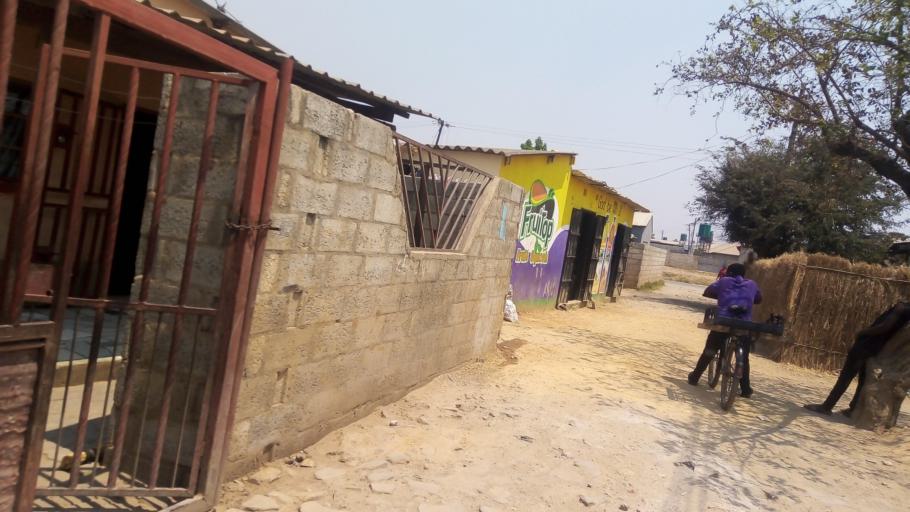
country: ZM
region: Lusaka
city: Lusaka
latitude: -15.4417
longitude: 28.3775
